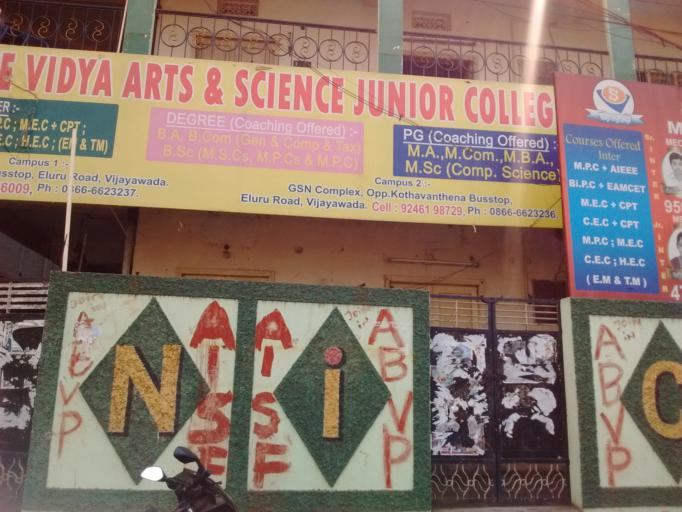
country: IN
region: Andhra Pradesh
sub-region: Krishna
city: Vijayawada
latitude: 16.5176
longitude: 80.6463
